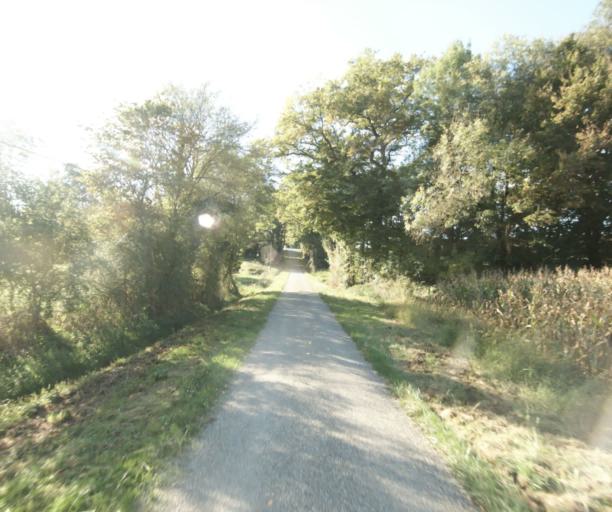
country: FR
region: Midi-Pyrenees
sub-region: Departement du Gers
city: Eauze
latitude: 43.7863
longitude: 0.1297
